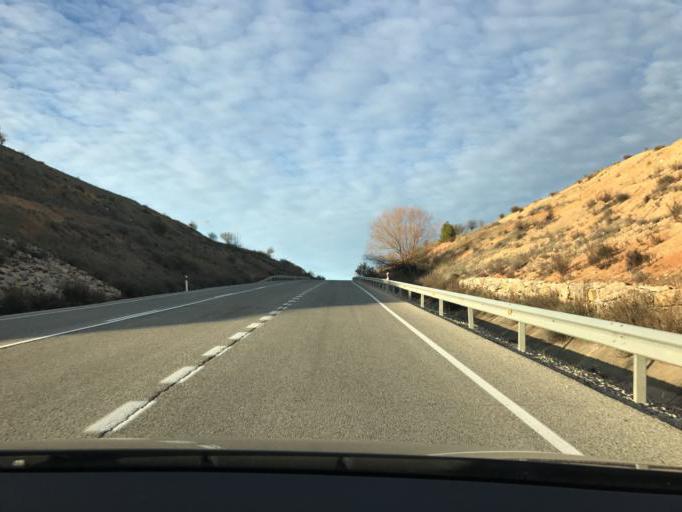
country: ES
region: Andalusia
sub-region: Provincia de Jaen
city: Guadahortuna
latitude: 37.5676
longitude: -3.4020
